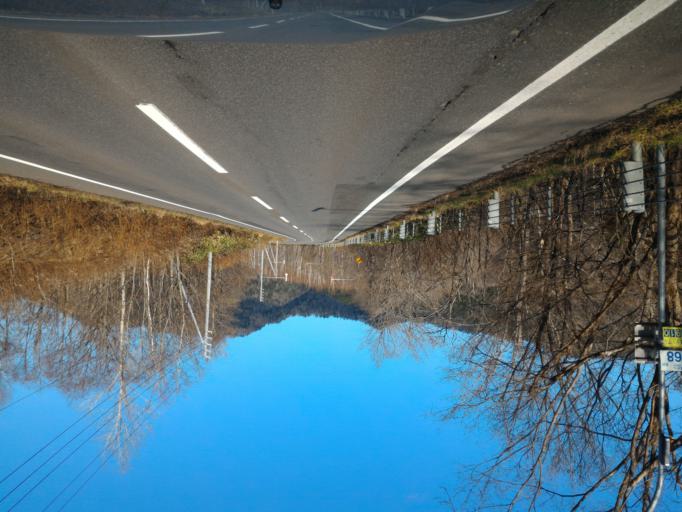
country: JP
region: Hokkaido
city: Ashibetsu
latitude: 43.3606
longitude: 142.1639
